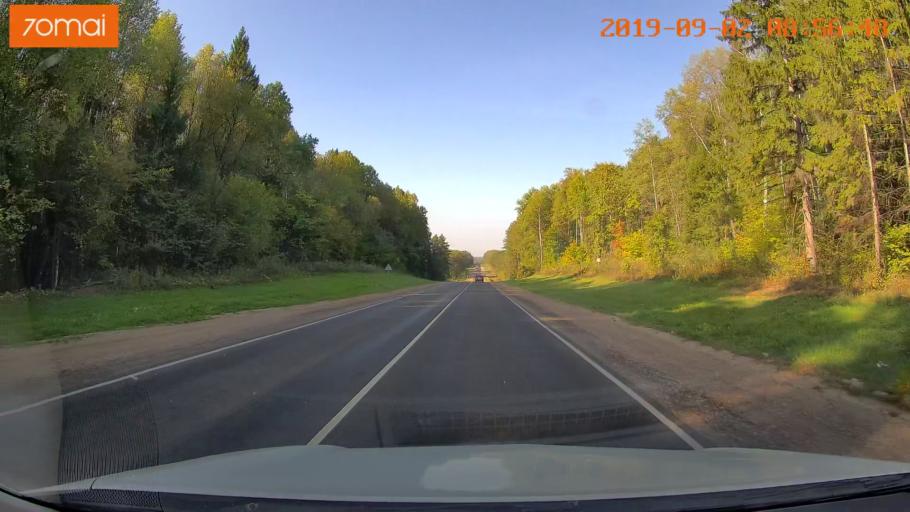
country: RU
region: Kaluga
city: Medyn'
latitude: 54.9423
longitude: 35.7839
